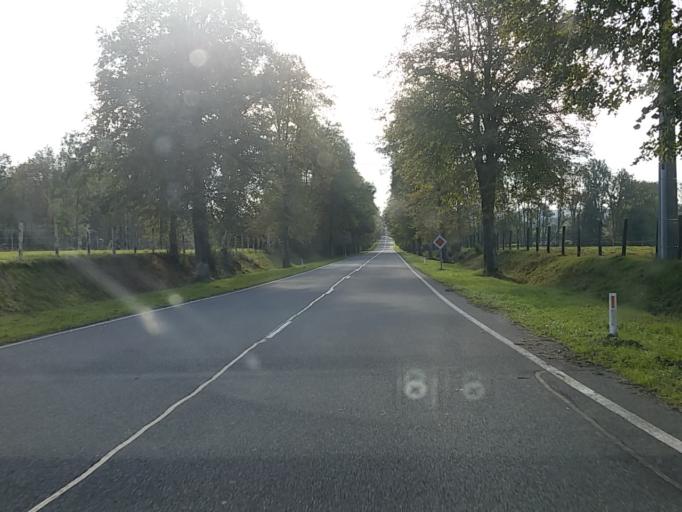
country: BE
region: Wallonia
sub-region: Province du Luxembourg
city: Herbeumont
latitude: 49.7354
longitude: 5.2275
